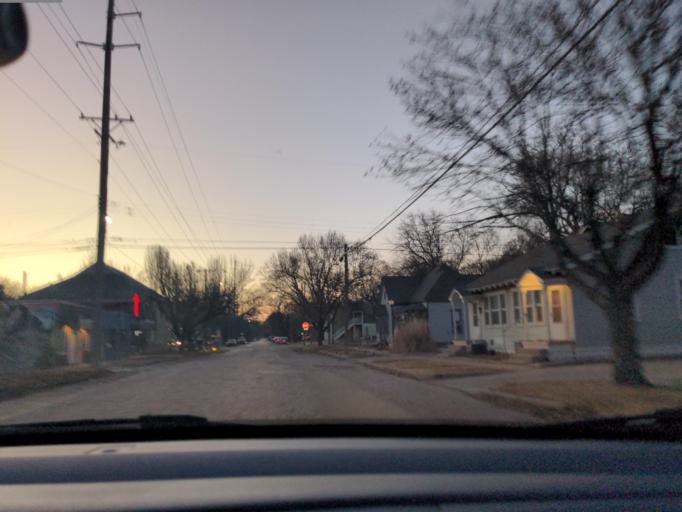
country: US
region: Kansas
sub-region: Sedgwick County
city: Wichita
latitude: 37.7044
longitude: -97.3473
